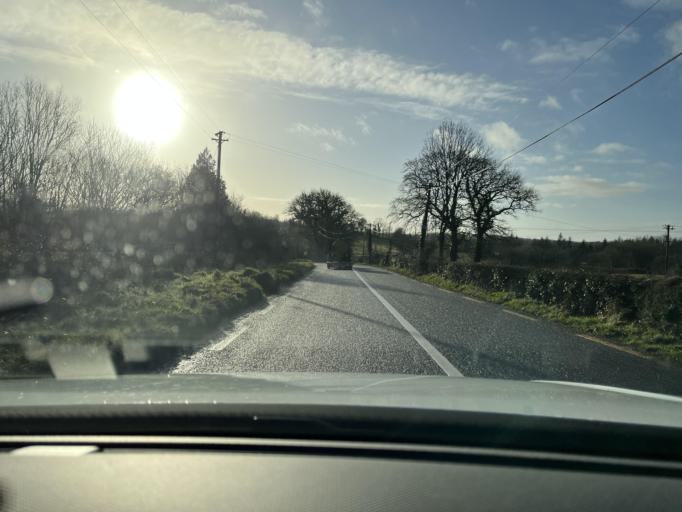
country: IE
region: Connaught
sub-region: County Leitrim
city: Manorhamilton
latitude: 54.2213
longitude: -8.2094
